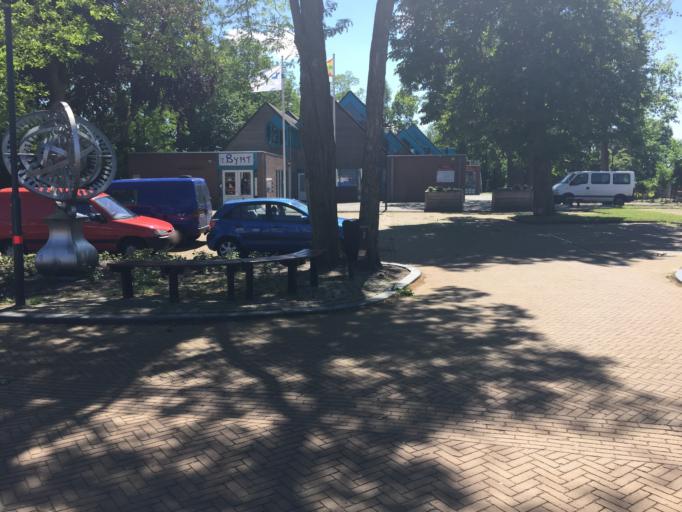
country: NL
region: Friesland
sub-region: Gemeente Smallingerland
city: Boornbergum
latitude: 53.0828
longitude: 6.0456
